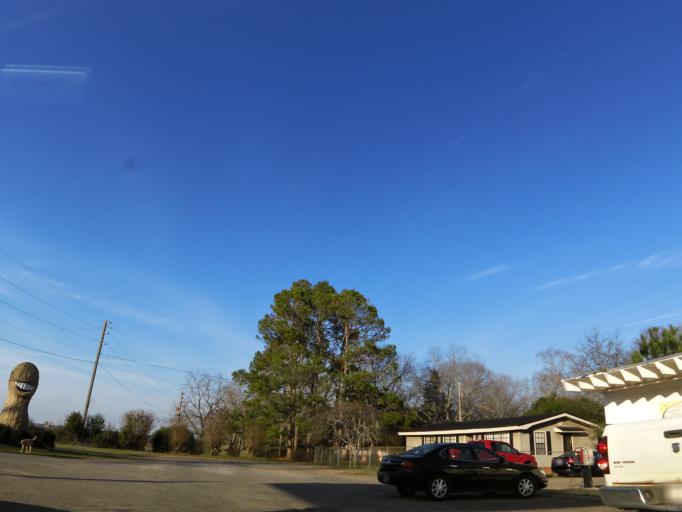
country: US
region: Georgia
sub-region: Webster County
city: Preston
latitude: 32.0415
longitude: -84.3923
